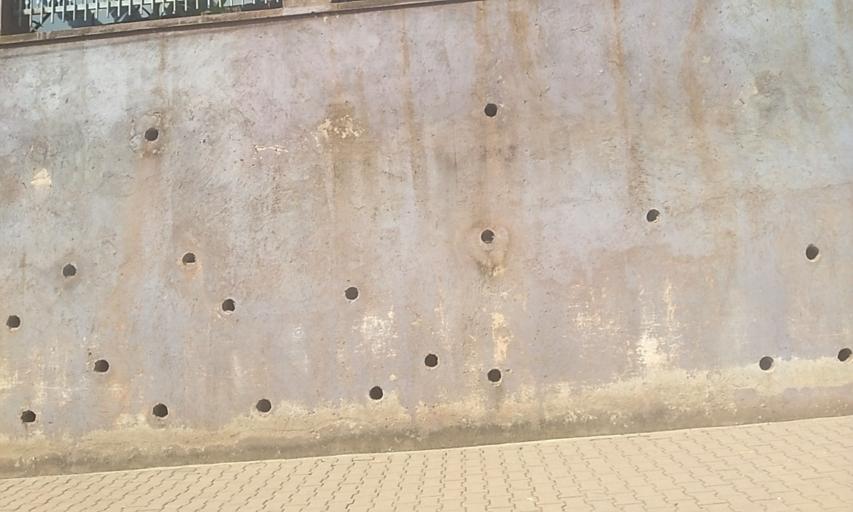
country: UG
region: Central Region
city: Kampala Central Division
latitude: 0.3370
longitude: 32.5816
